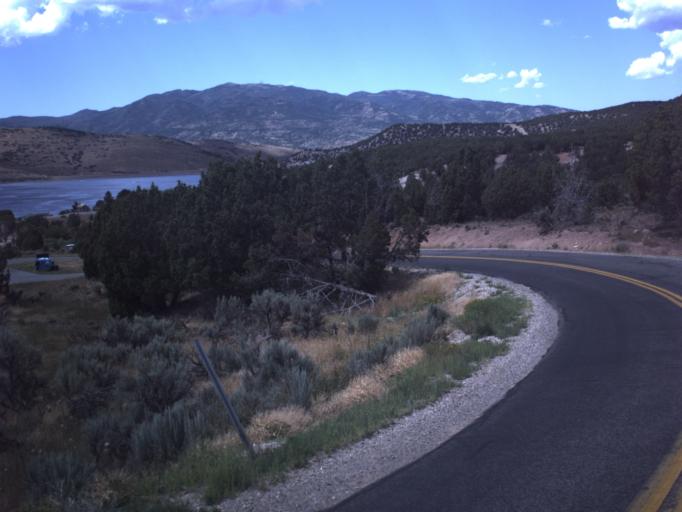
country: US
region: Utah
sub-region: Summit County
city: Oakley
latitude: 40.7742
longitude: -111.3860
